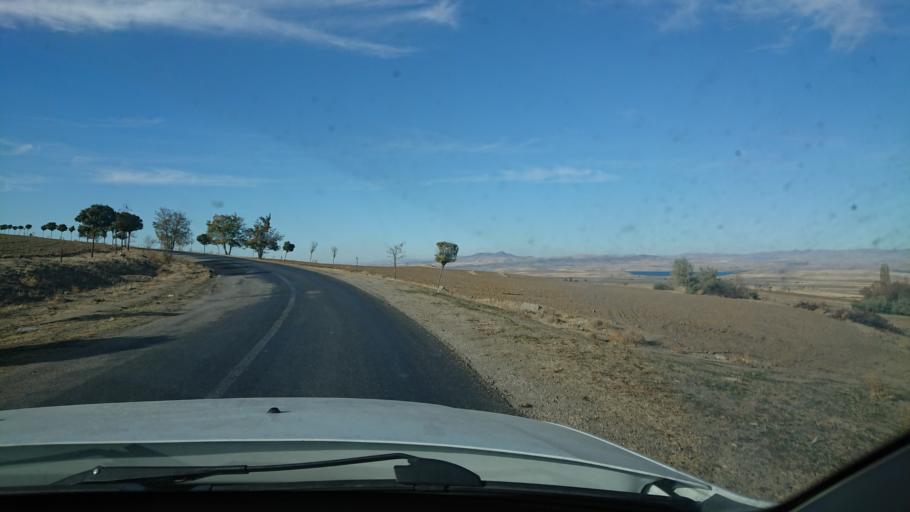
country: TR
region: Aksaray
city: Sariyahsi
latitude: 38.9707
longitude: 33.8663
